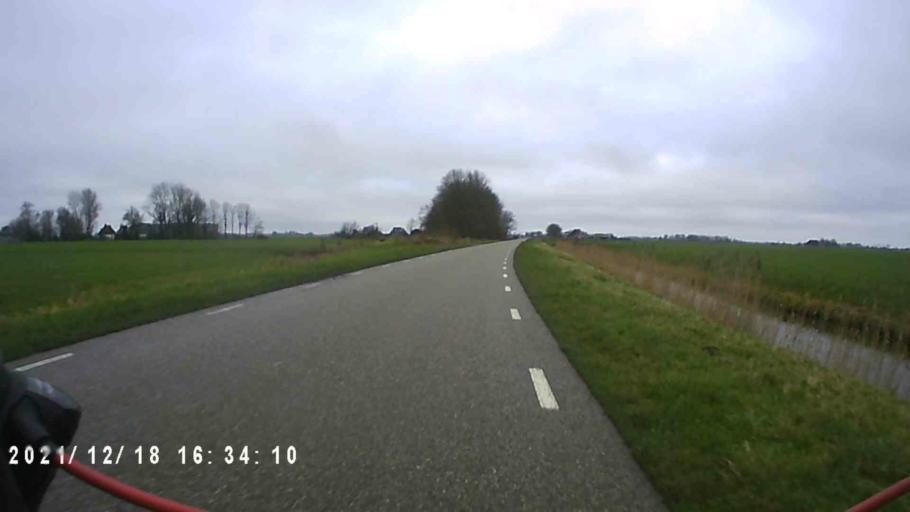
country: NL
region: Friesland
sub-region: Gemeente Dongeradeel
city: Dokkum
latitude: 53.3567
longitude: 6.0255
